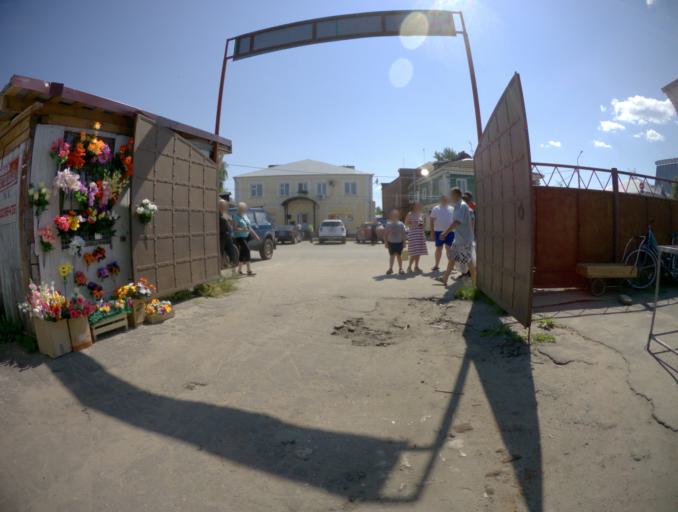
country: RU
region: Vladimir
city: Vyazniki
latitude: 56.2474
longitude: 42.1596
